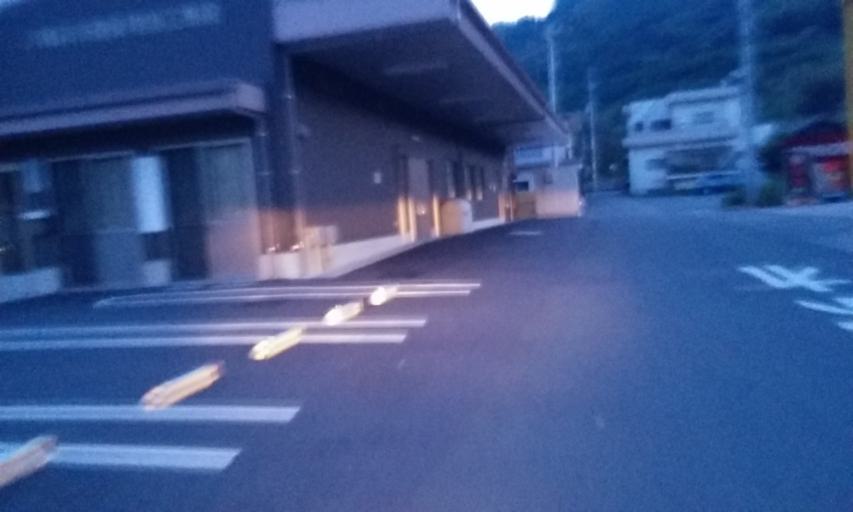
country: JP
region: Ehime
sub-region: Nishiuwa-gun
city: Ikata-cho
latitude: 33.4888
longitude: 132.3988
